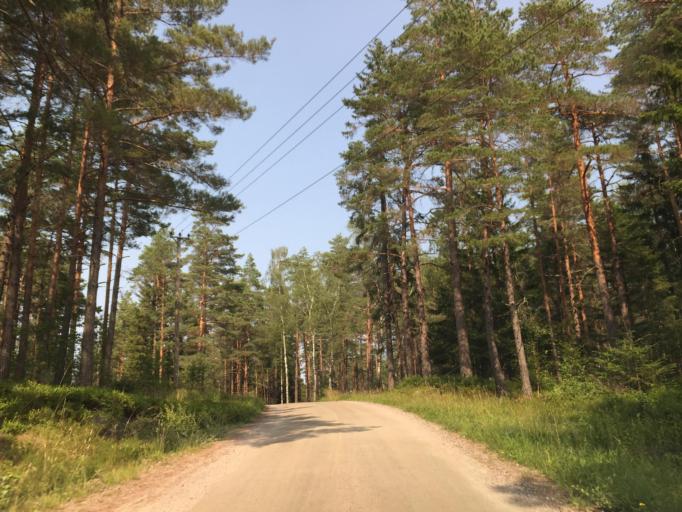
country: SE
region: Vaestra Goetaland
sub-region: Lilla Edets Kommun
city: Lilla Edet
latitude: 58.2505
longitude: 12.0893
